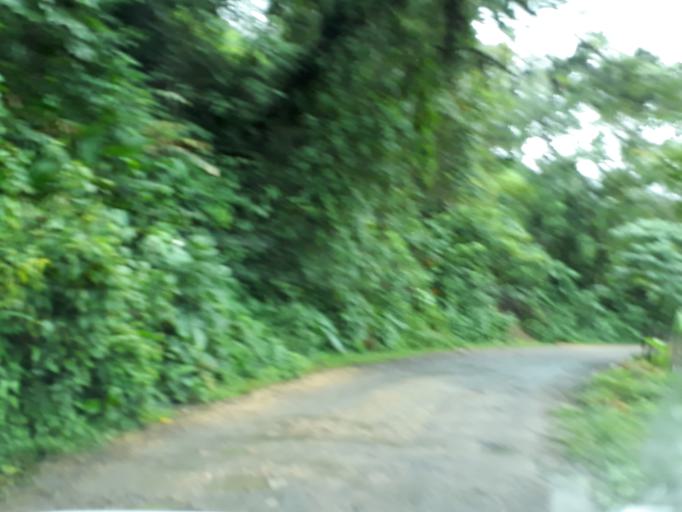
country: CO
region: Boyaca
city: Santa Maria
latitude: 4.7569
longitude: -73.3148
